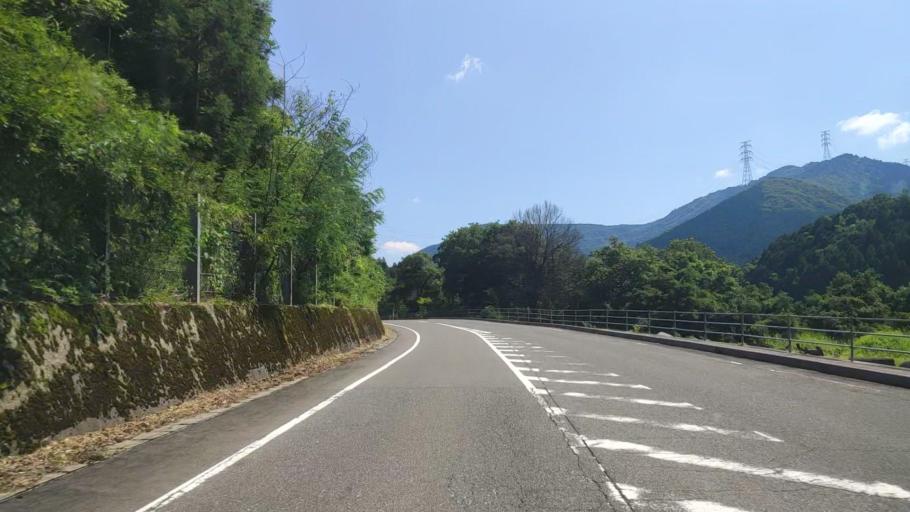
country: JP
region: Gifu
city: Godo
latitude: 35.5979
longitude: 136.6285
